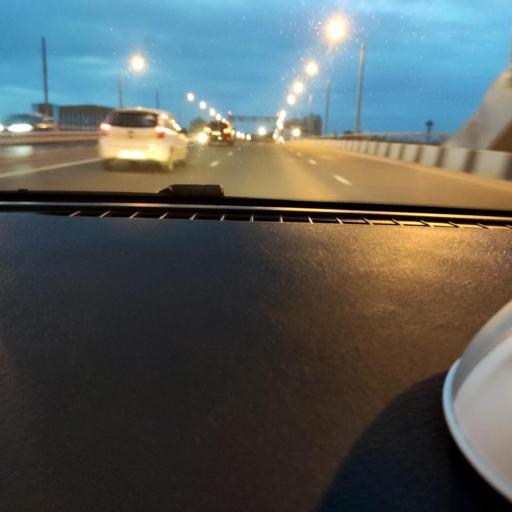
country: RU
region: Samara
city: Rozhdestveno
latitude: 53.1738
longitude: 50.0859
